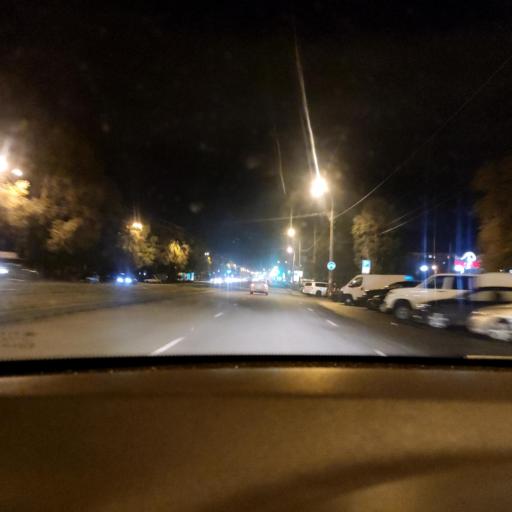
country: RU
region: Samara
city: Samara
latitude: 53.2145
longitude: 50.2250
